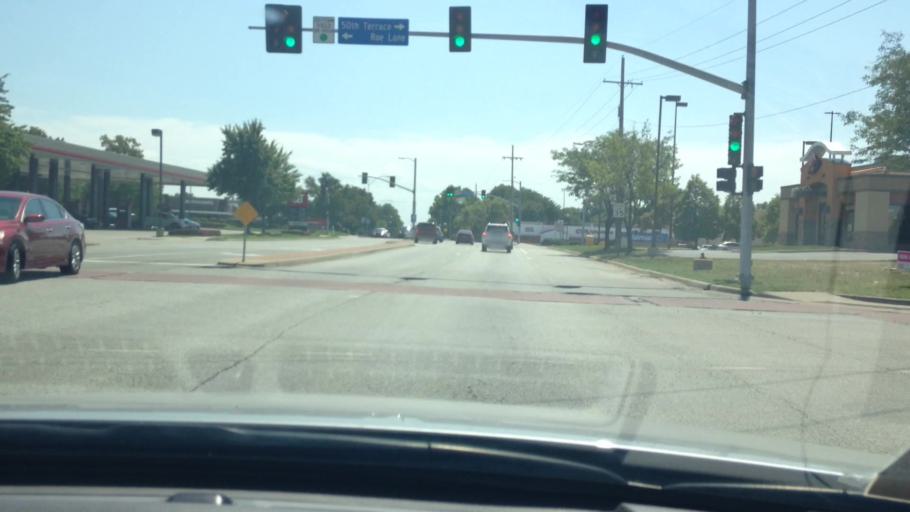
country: US
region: Kansas
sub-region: Johnson County
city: Roeland Park
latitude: 39.0377
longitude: -94.6397
